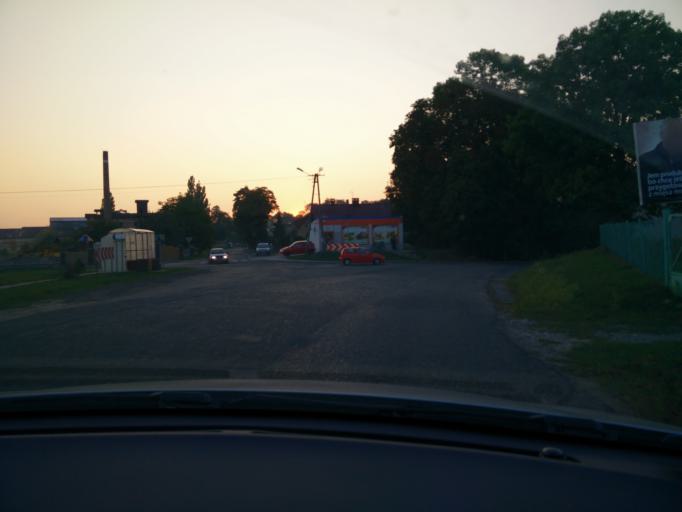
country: PL
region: Greater Poland Voivodeship
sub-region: Powiat sredzki
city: Dominowo
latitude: 52.2128
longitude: 17.3840
